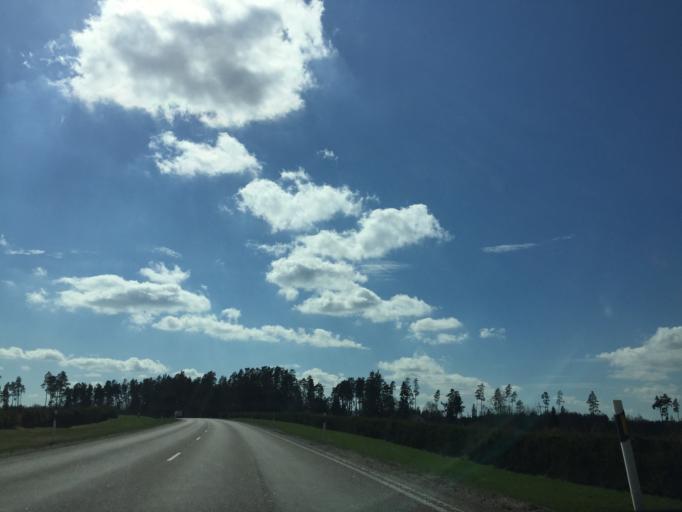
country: EE
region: Tartu
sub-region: Elva linn
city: Elva
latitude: 58.0873
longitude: 26.2141
